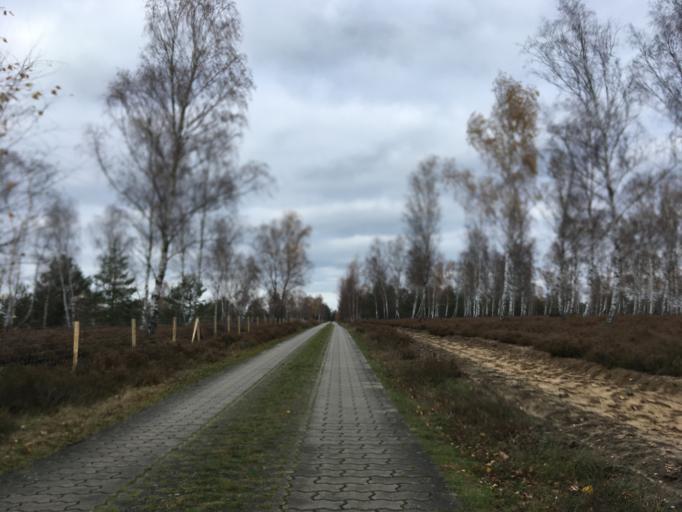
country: DE
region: Brandenburg
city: Tauer
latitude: 52.0029
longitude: 14.5042
